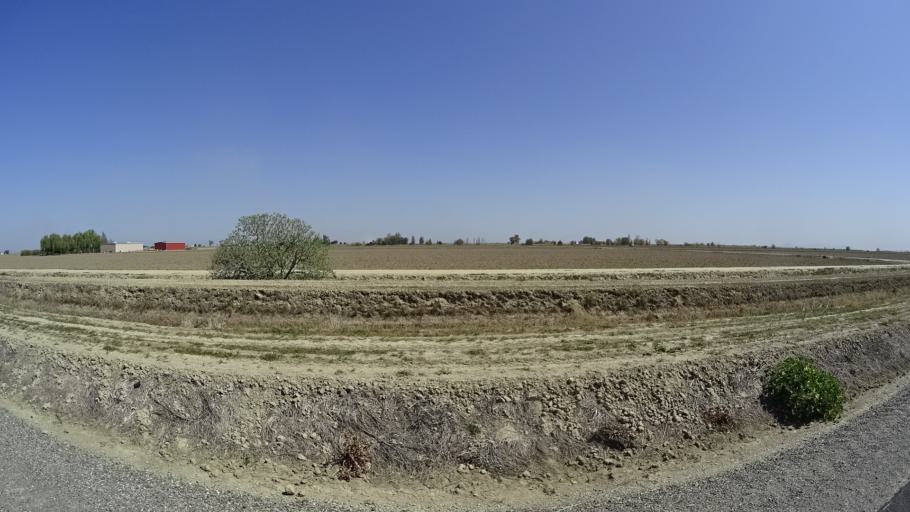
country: US
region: California
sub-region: Glenn County
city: Willows
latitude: 39.5281
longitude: -122.1369
